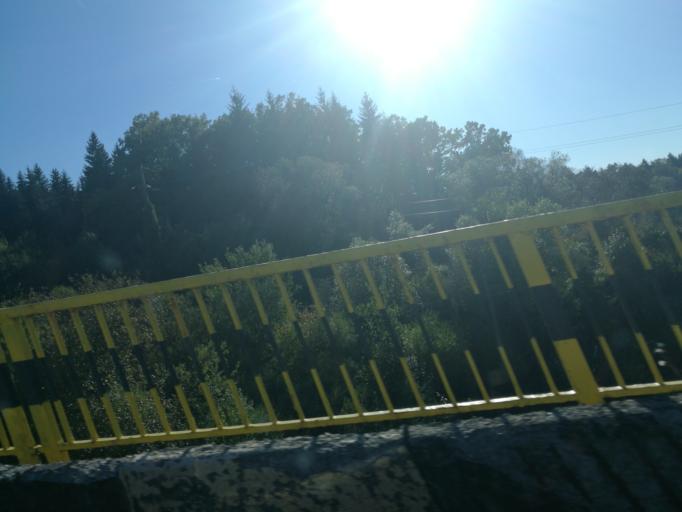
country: RO
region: Brasov
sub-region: Comuna Dumbravita
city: Dumbravita
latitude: 45.7639
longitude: 25.3778
